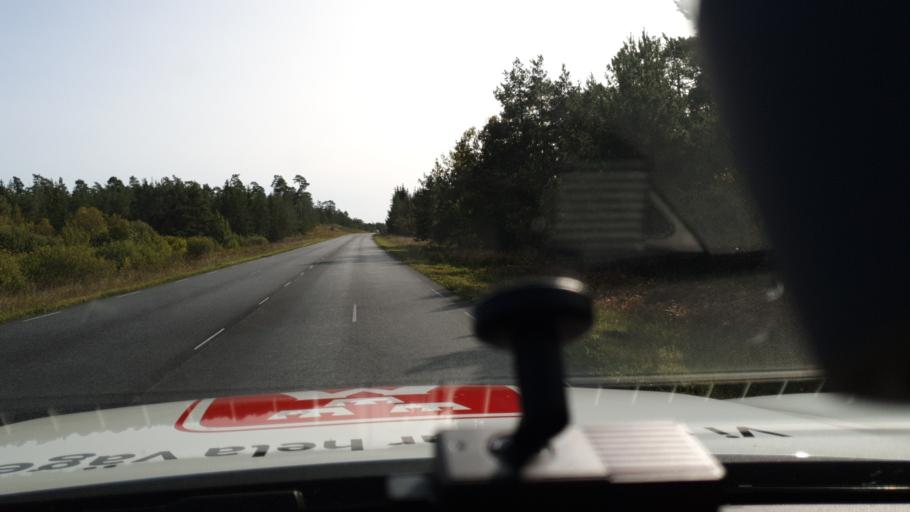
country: SE
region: Gotland
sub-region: Gotland
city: Slite
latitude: 57.7409
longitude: 18.7902
